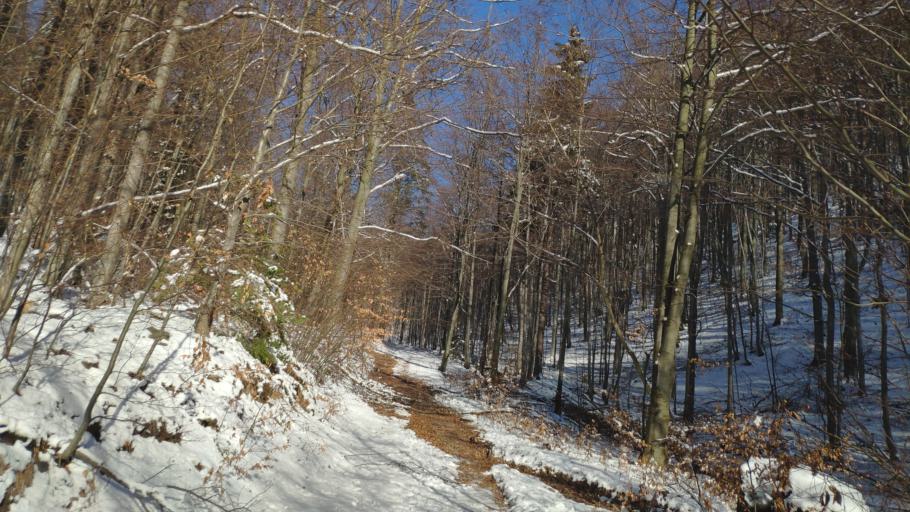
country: SK
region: Kosicky
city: Gelnica
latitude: 48.7616
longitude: 21.0088
